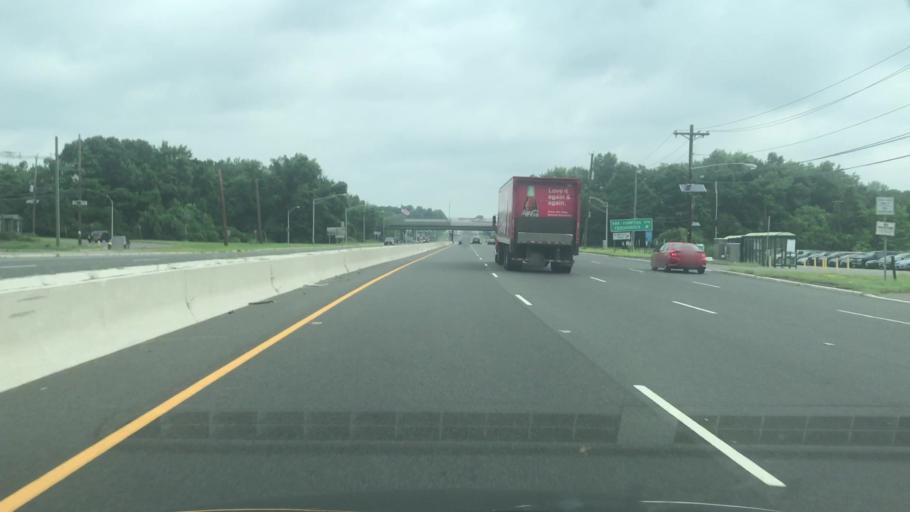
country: US
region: New Jersey
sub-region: Passaic County
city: Wayne
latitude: 40.9220
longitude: -74.2680
